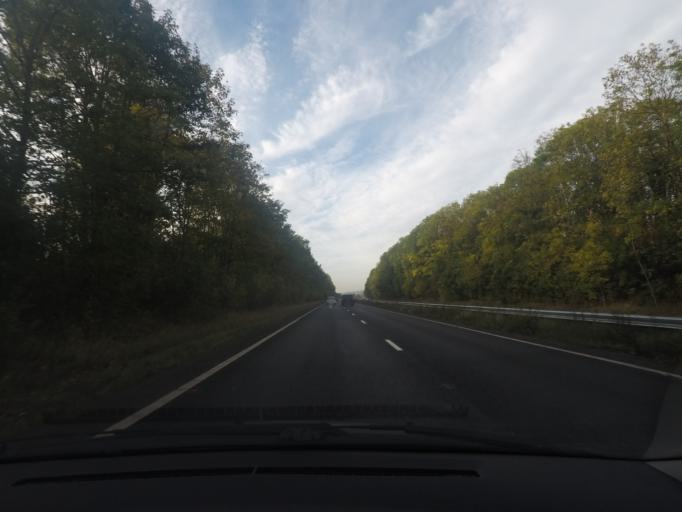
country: GB
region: England
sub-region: North Yorkshire
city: Tadcaster
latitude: 53.8840
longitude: -1.2511
